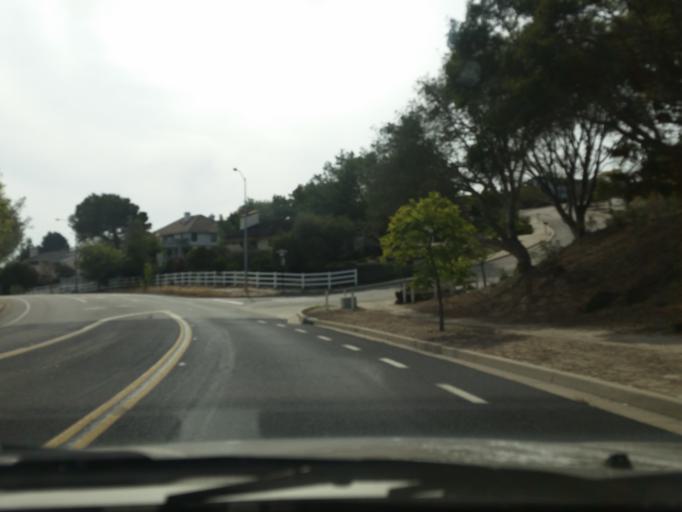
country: US
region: California
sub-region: San Luis Obispo County
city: Arroyo Grande
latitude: 35.1340
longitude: -120.5980
